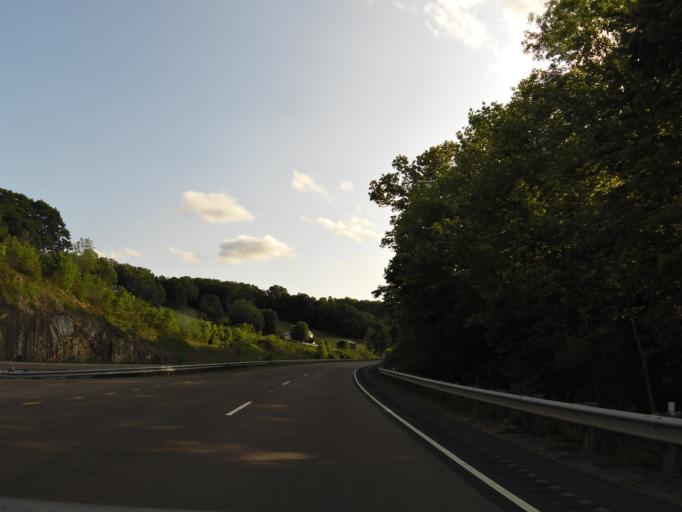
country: US
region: Virginia
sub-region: Tazewell County
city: Raven
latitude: 36.9841
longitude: -81.8541
